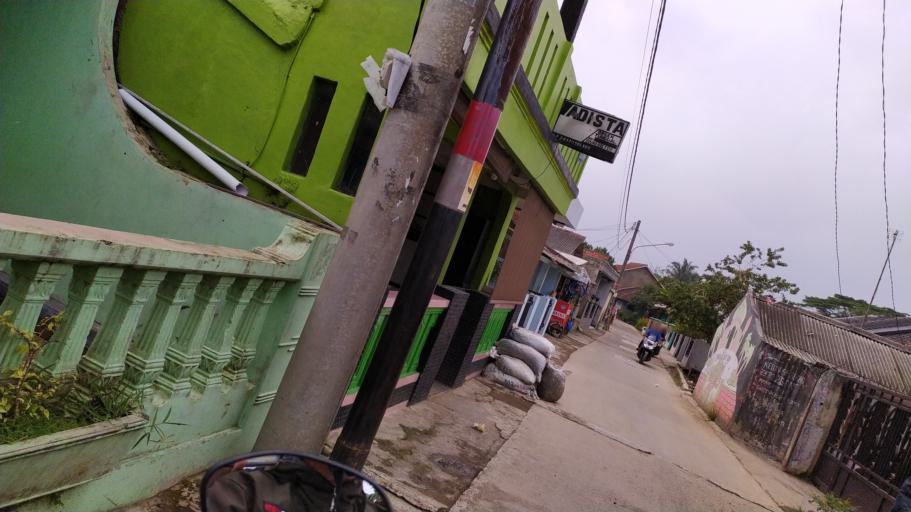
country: ID
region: West Java
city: Ciampea
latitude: -6.5807
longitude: 106.7237
